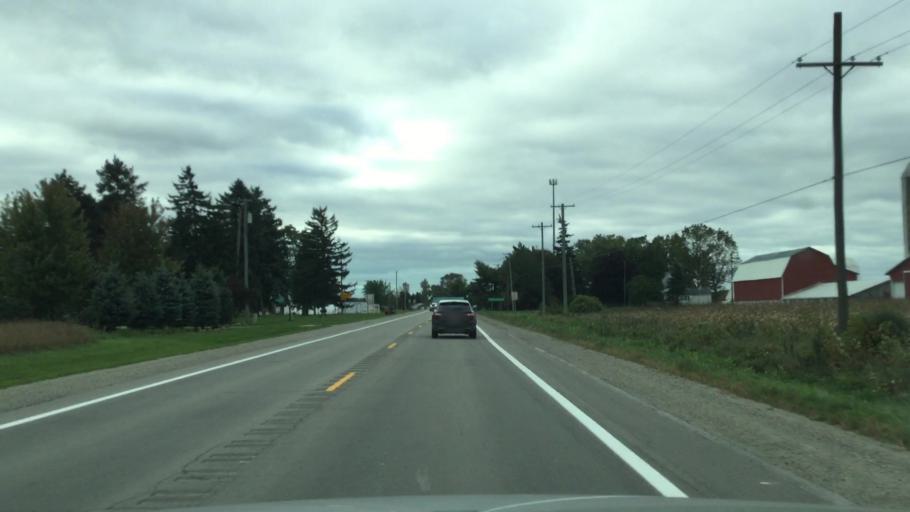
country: US
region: Michigan
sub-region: Macomb County
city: Memphis
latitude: 42.8641
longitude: -82.7672
